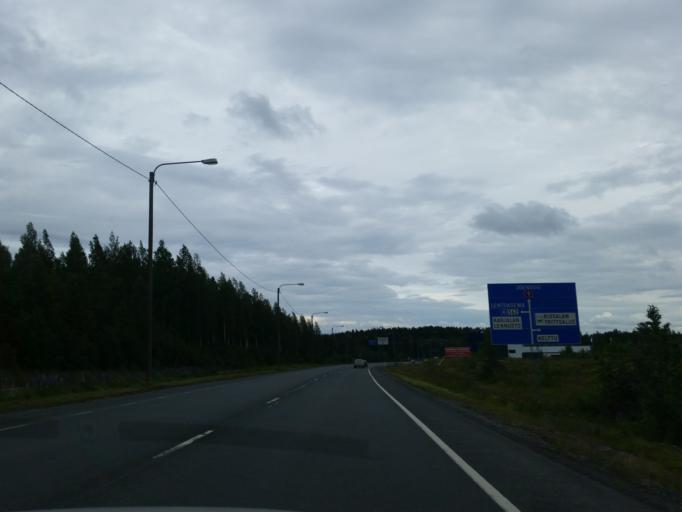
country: FI
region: Northern Savo
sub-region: Kuopio
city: Kuopio
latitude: 62.9858
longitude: 27.7635
